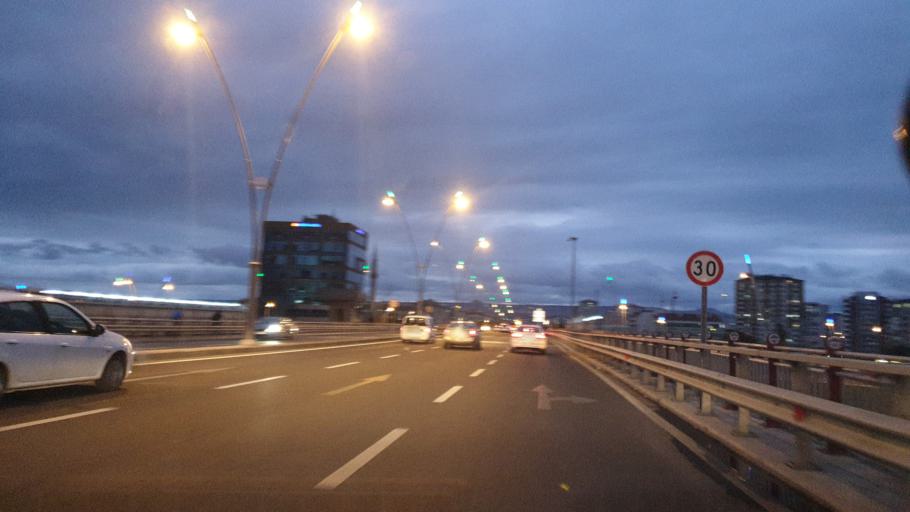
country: TR
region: Kayseri
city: Kayseri
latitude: 38.7336
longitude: 35.4942
